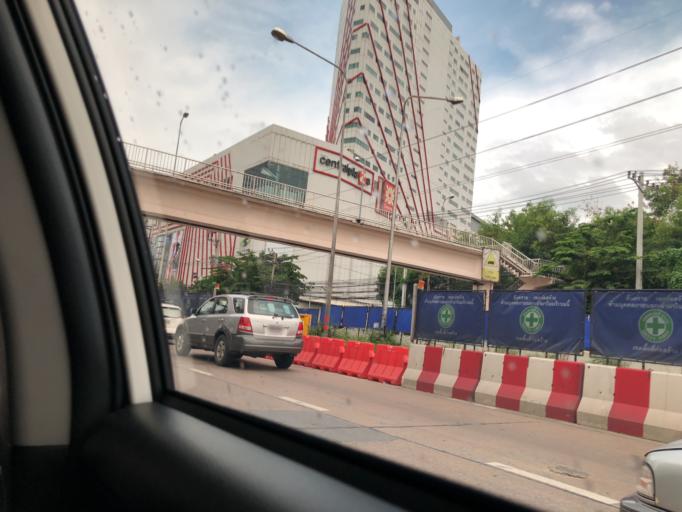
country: TH
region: Nonthaburi
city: Pak Kret
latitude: 13.9051
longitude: 100.5267
